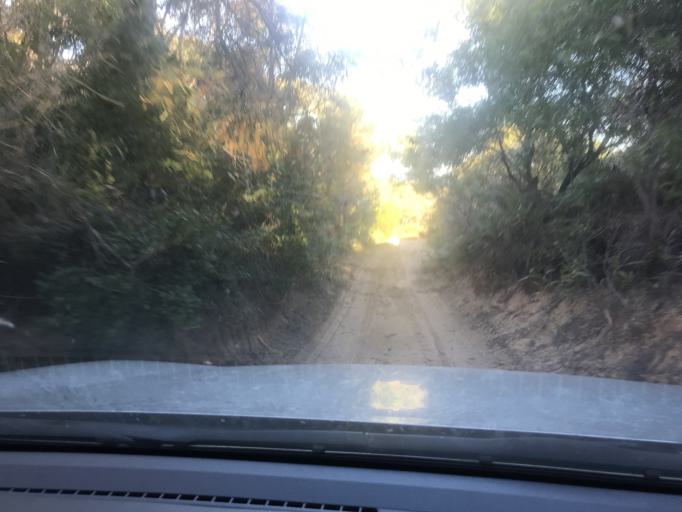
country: AU
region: Queensland
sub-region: Fraser Coast
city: Urangan
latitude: -25.3900
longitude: 153.1752
